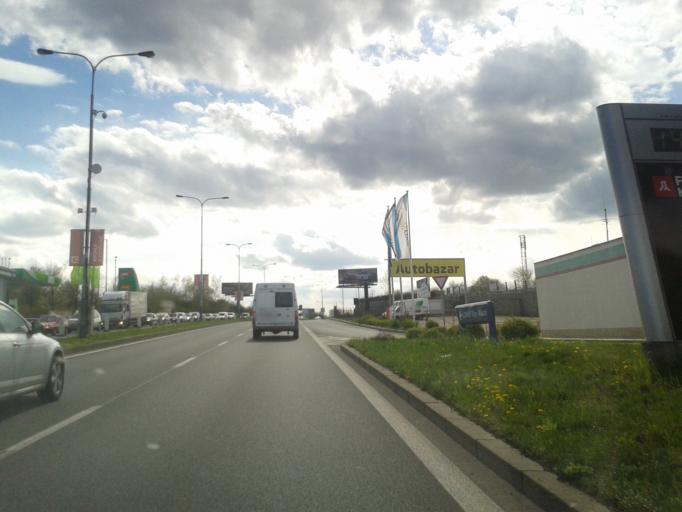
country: CZ
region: Praha
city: Branik
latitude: 50.0309
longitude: 14.3807
